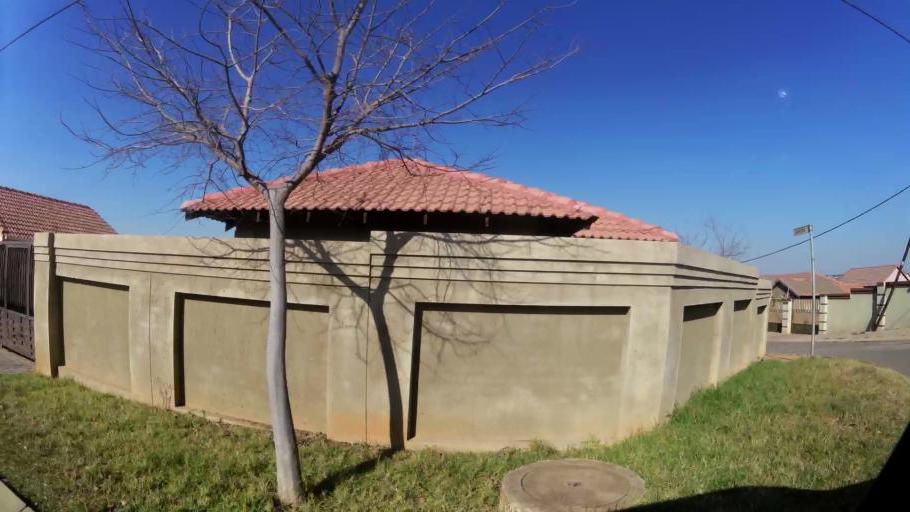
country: ZA
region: Gauteng
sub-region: West Rand District Municipality
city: Muldersdriseloop
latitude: -26.0341
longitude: 27.9143
